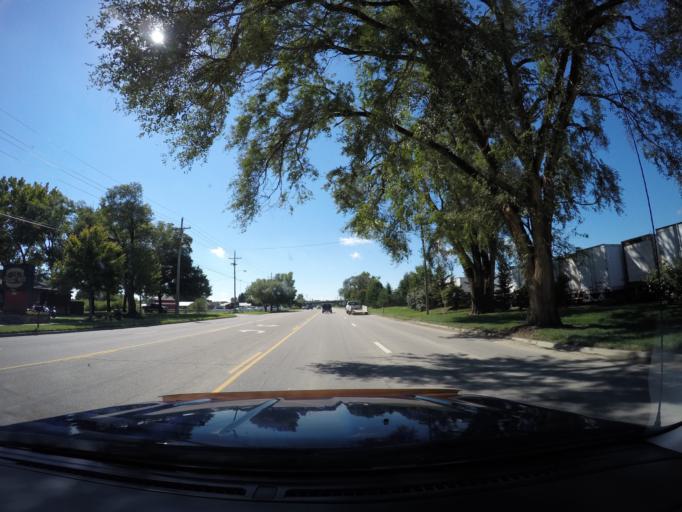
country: US
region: Kansas
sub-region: Douglas County
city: Lawrence
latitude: 38.9964
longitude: -95.2334
